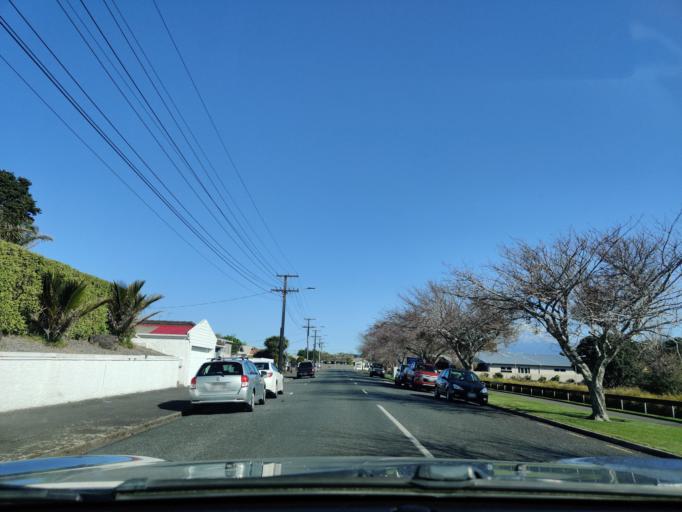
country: NZ
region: Taranaki
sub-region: New Plymouth District
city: New Plymouth
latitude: -39.0722
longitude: 174.0579
